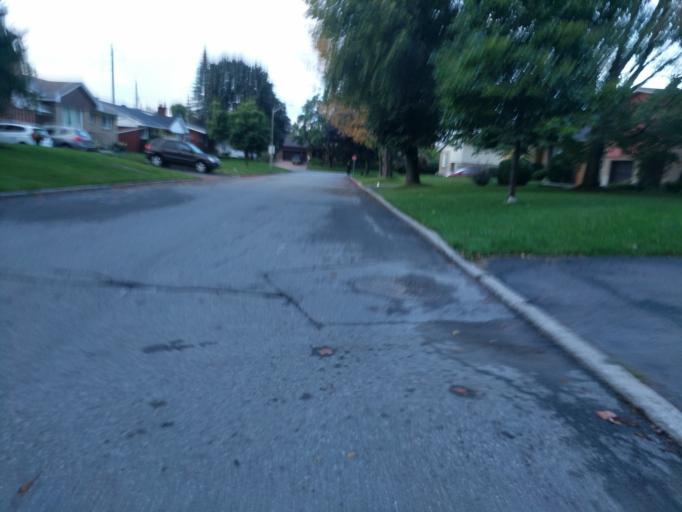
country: CA
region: Ontario
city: Ottawa
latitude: 45.3601
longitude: -75.7590
